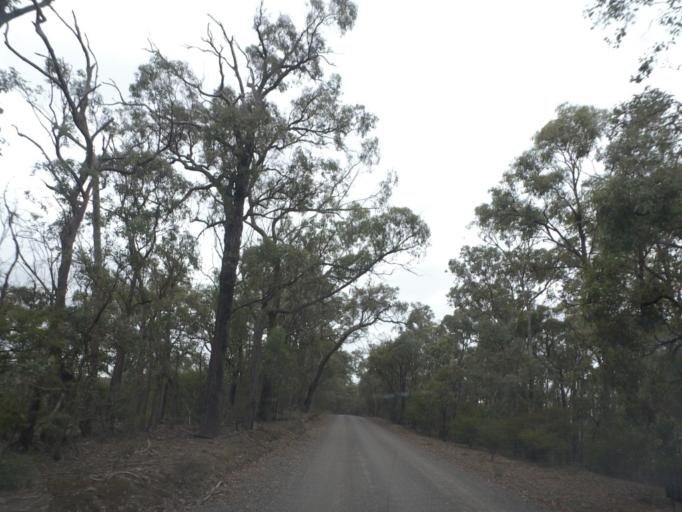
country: AU
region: Victoria
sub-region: Yarra Ranges
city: Chirnside Park
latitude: -37.6841
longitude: 145.3198
